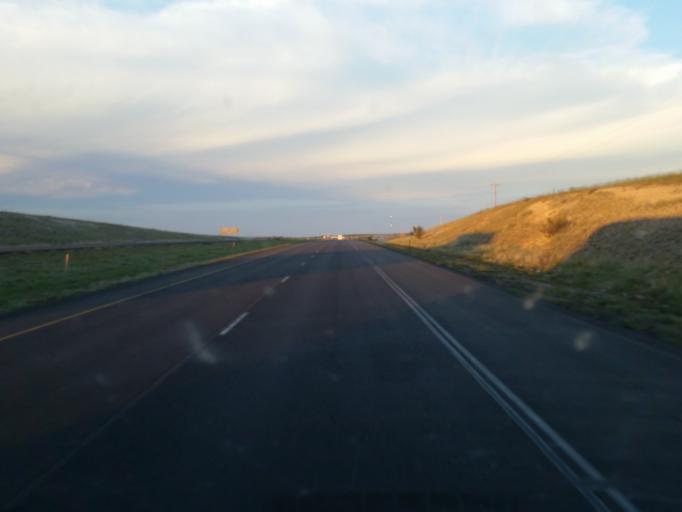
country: US
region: New Mexico
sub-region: Guadalupe County
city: Santa Rosa
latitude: 34.9898
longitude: -105.2622
